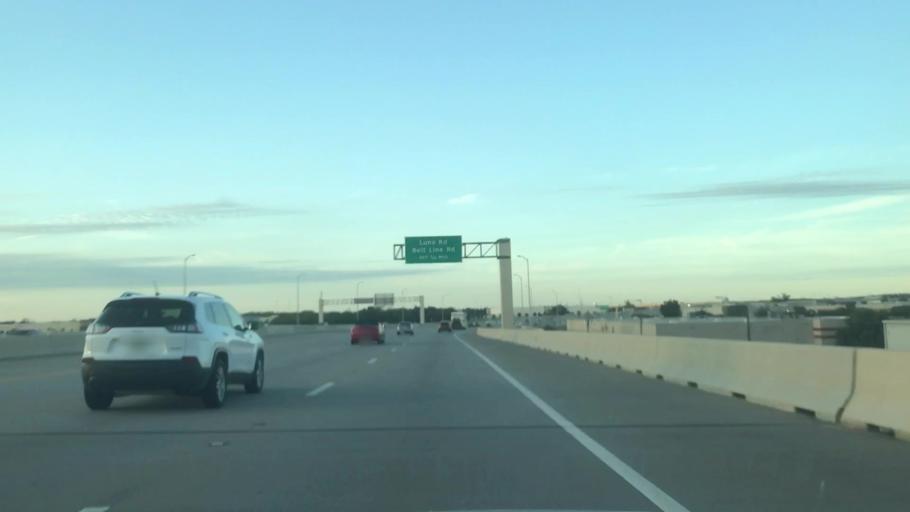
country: US
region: Texas
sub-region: Dallas County
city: Farmers Branch
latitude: 32.9397
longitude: -96.9298
